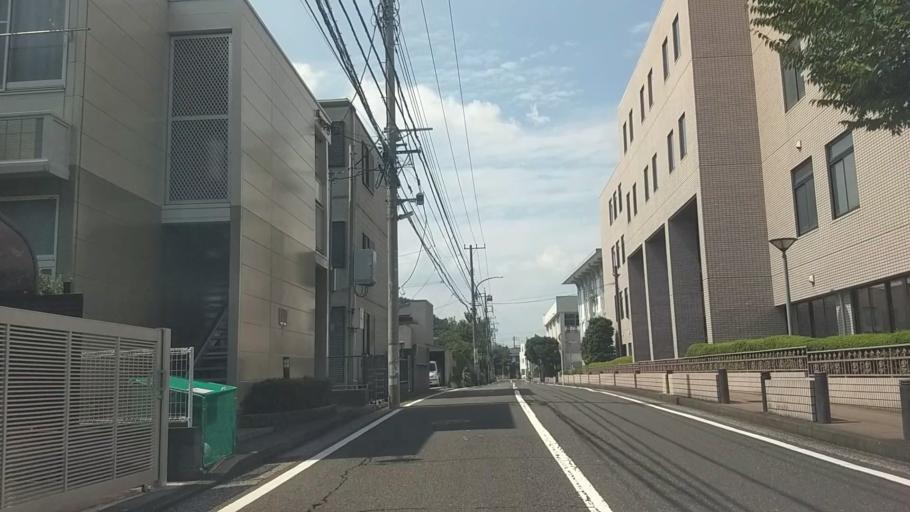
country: JP
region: Kanagawa
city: Yokohama
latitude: 35.4806
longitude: 139.6203
